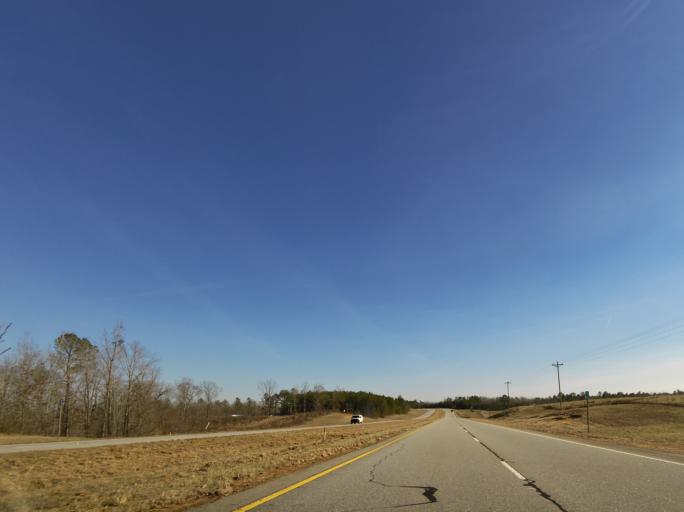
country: US
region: Georgia
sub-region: Upson County
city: Thomaston
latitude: 32.7487
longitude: -84.2389
